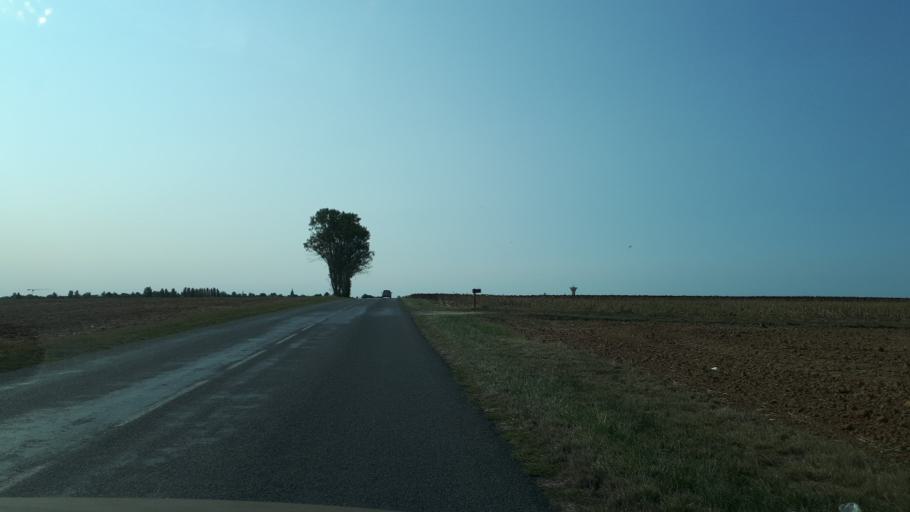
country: FR
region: Centre
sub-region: Departement du Cher
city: Rians
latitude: 47.1948
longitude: 2.5969
